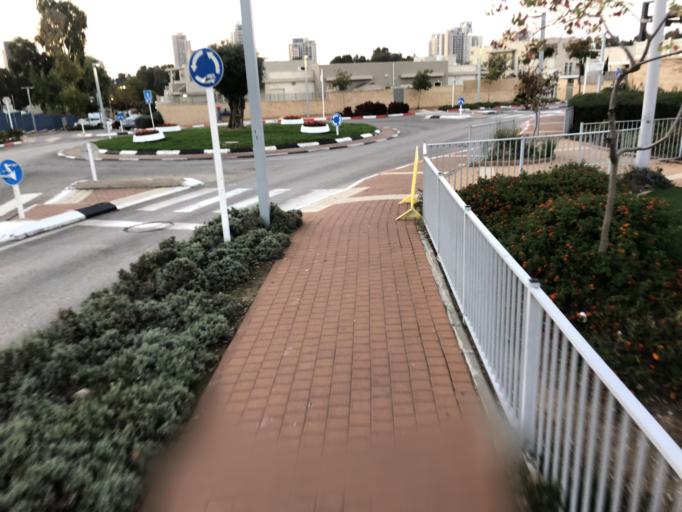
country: IL
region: Northern District
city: `Akko
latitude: 32.9341
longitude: 35.0901
